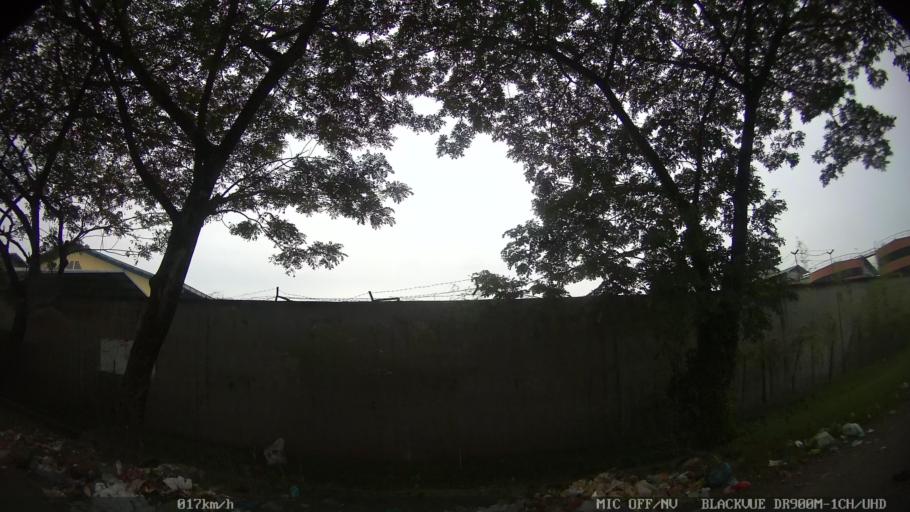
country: ID
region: North Sumatra
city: Deli Tua
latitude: 3.5380
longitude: 98.7283
